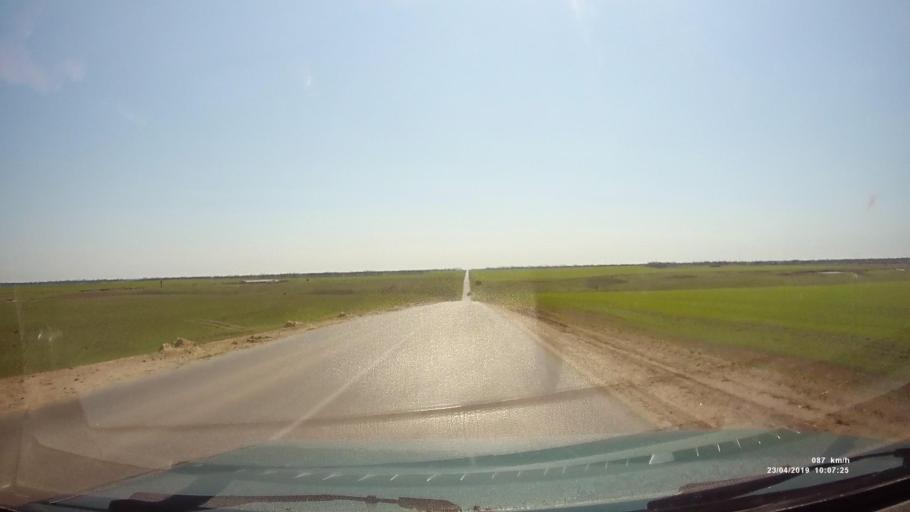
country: RU
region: Rostov
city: Sovetskoye
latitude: 46.7261
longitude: 42.2512
